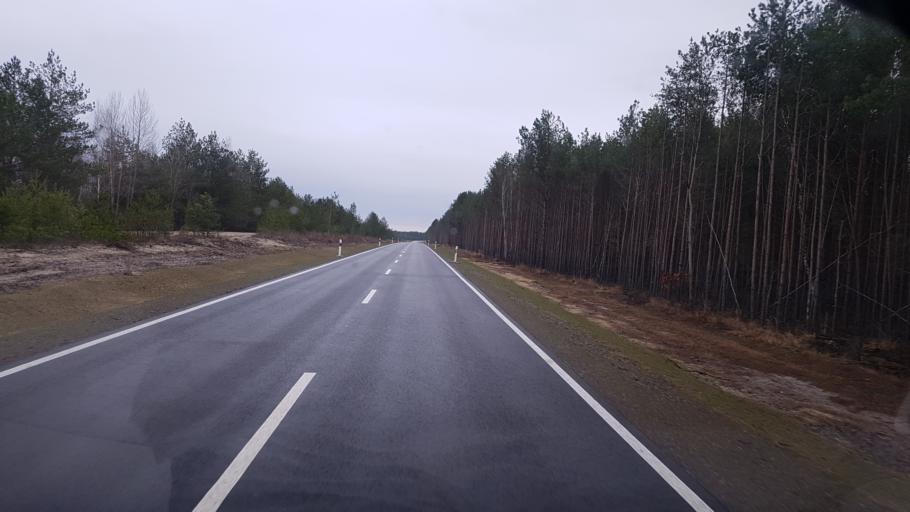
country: DE
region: Brandenburg
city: Lauchhammer
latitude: 51.5318
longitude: 13.7740
